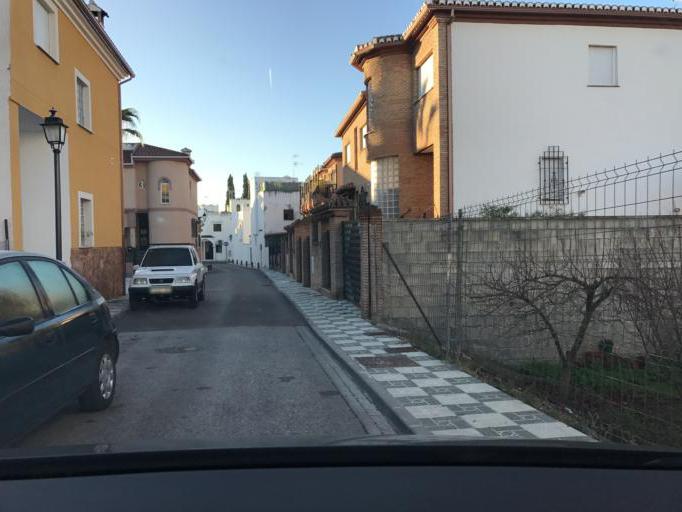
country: ES
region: Andalusia
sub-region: Provincia de Granada
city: Pulianas
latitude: 37.2190
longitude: -3.6026
